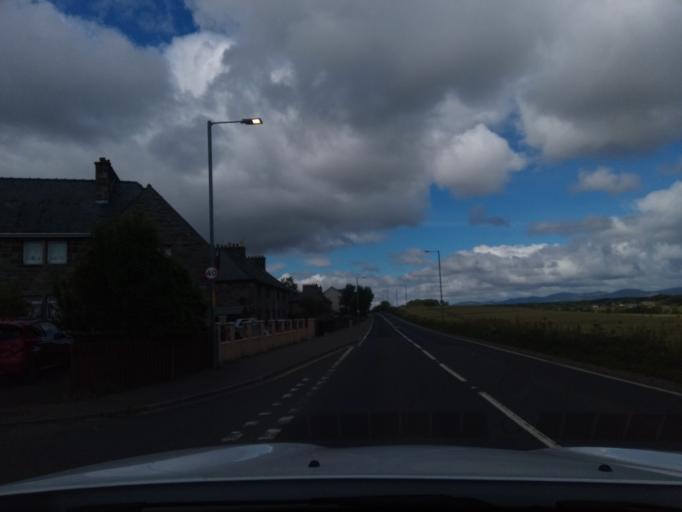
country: GB
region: Scotland
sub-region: Fife
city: Cairneyhill
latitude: 56.0493
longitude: -3.5276
